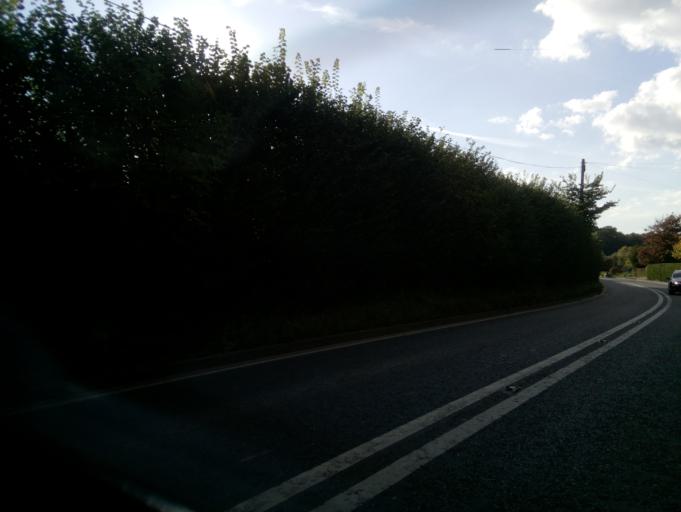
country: GB
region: England
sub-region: Herefordshire
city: Credenhill
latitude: 52.0728
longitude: -2.7847
